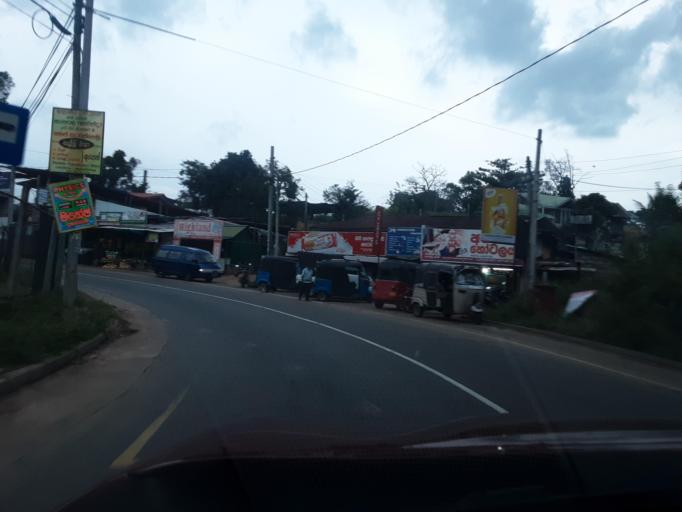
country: LK
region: Central
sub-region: Nuwara Eliya District
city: Nuwara Eliya
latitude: 6.9023
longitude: 80.9007
